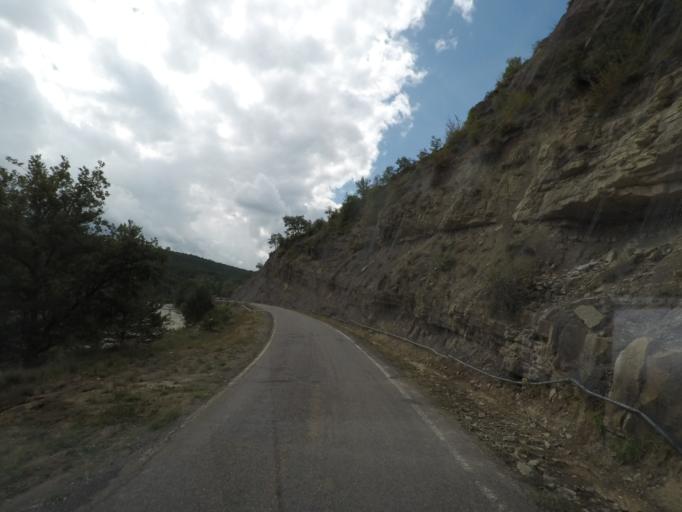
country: ES
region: Aragon
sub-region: Provincia de Huesca
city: Yebra de Basa
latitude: 42.4033
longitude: -0.2470
